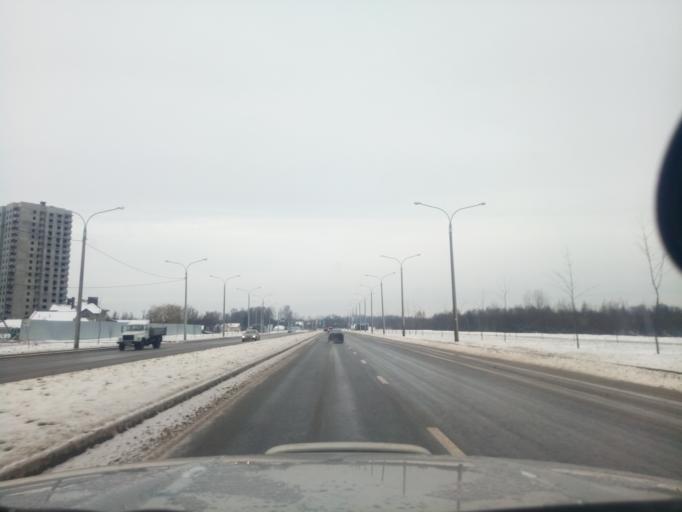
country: BY
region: Minsk
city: Machulishchy
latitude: 53.8388
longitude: 27.5960
